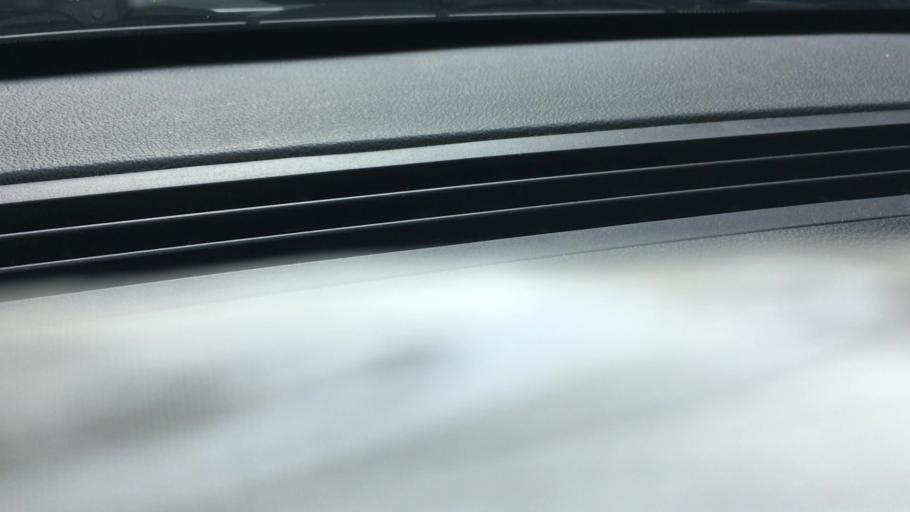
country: US
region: Alabama
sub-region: Shelby County
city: Helena
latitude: 33.2433
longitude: -86.9601
